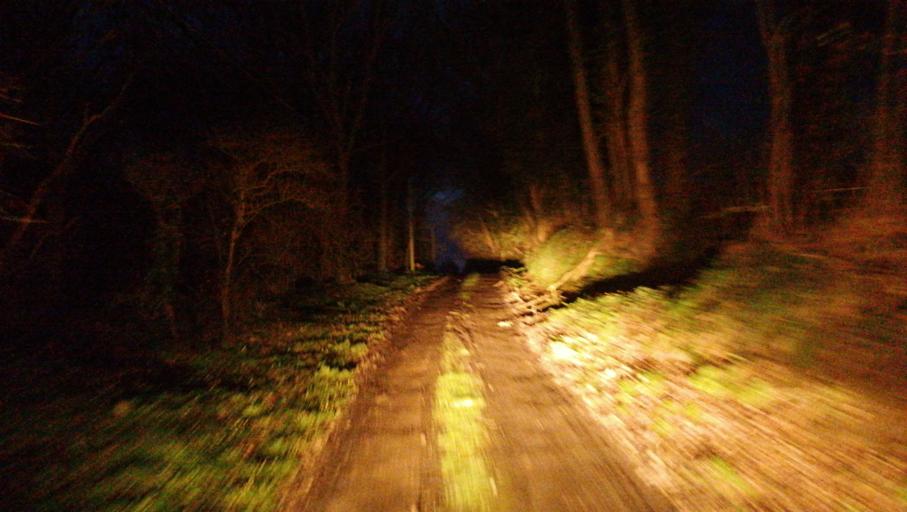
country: FR
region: Brittany
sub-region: Departement des Cotes-d'Armor
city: Plehedel
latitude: 48.6835
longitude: -3.0333
